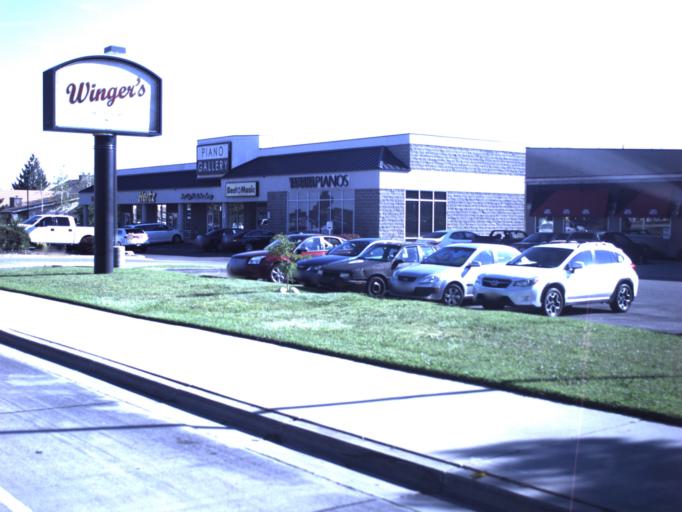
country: US
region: Utah
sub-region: Utah County
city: Orem
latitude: 40.2861
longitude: -111.6903
